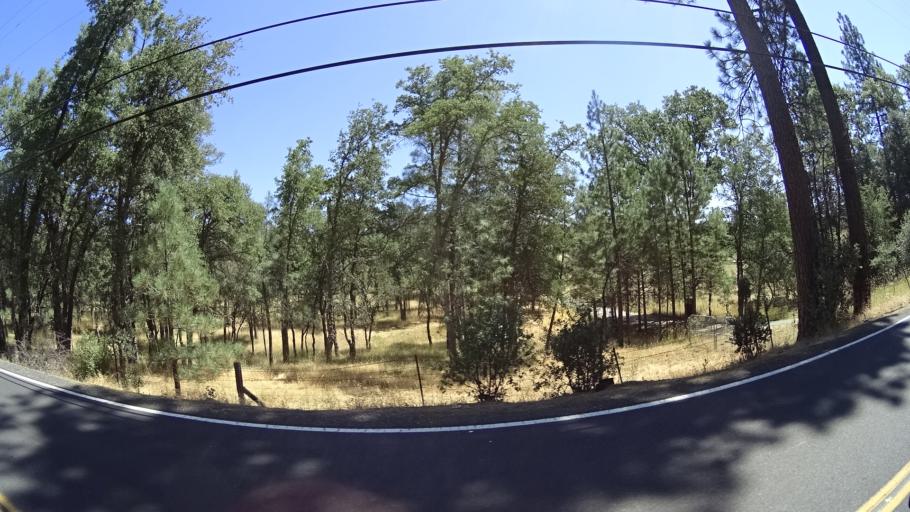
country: US
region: California
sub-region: Calaveras County
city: Mountain Ranch
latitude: 38.2465
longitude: -120.5179
